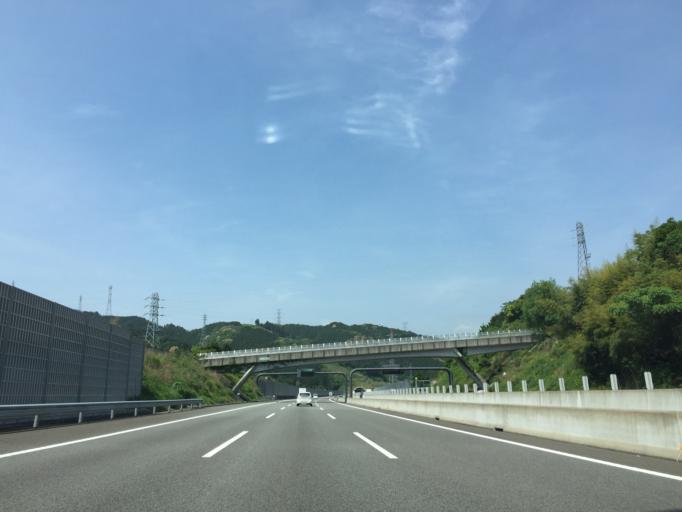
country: JP
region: Shizuoka
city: Kanaya
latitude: 34.8462
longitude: 138.1101
